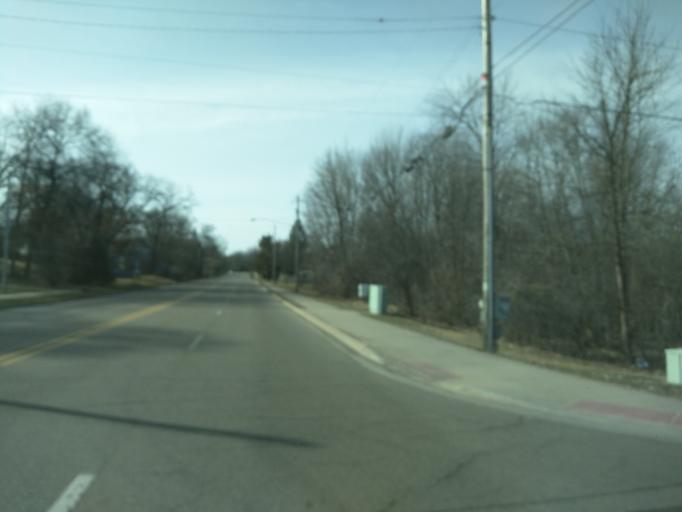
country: US
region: Michigan
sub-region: Ingham County
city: Haslett
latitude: 42.7663
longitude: -84.4130
